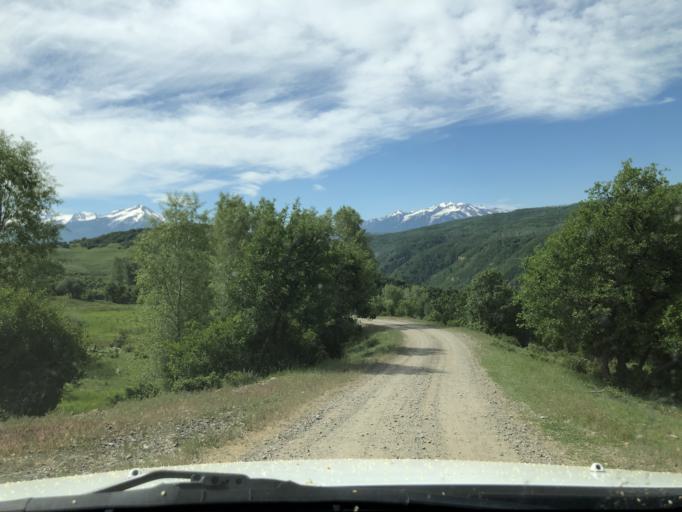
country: US
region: Colorado
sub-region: Delta County
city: Paonia
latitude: 39.0005
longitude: -107.3461
